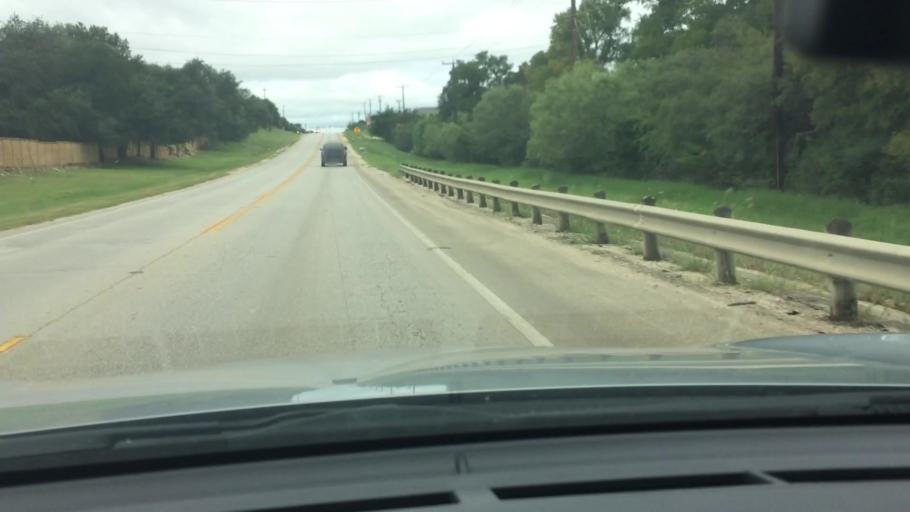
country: US
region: Texas
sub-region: Comal County
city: Garden Ridge
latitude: 29.6441
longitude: -98.3967
